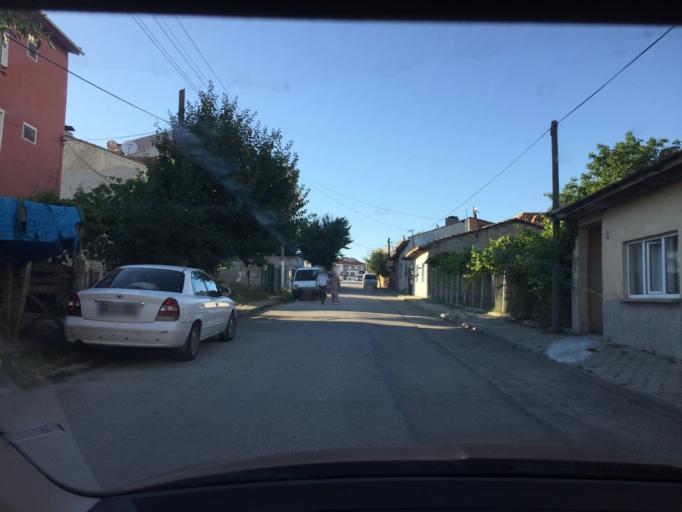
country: TR
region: Eskisehir
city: Eskisehir
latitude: 39.7760
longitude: 30.4529
